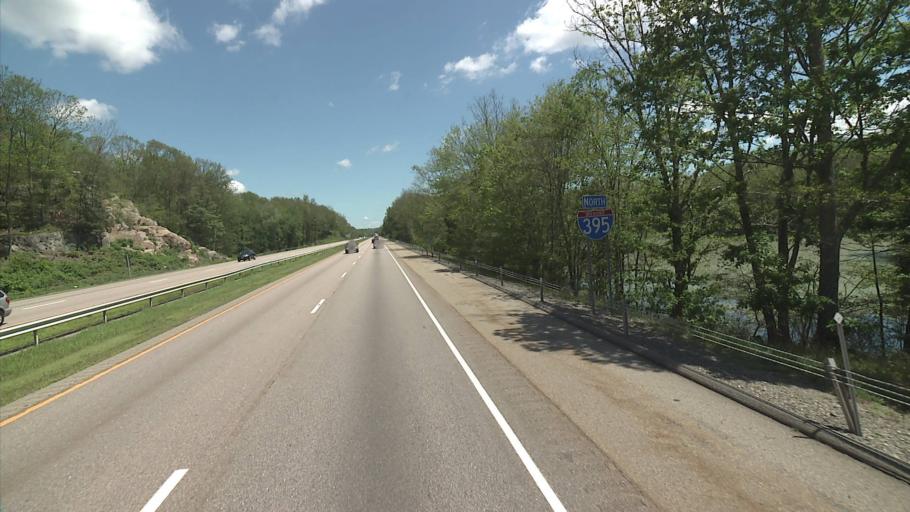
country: US
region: Connecticut
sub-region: New London County
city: Oxoboxo River
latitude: 41.4144
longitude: -72.1382
